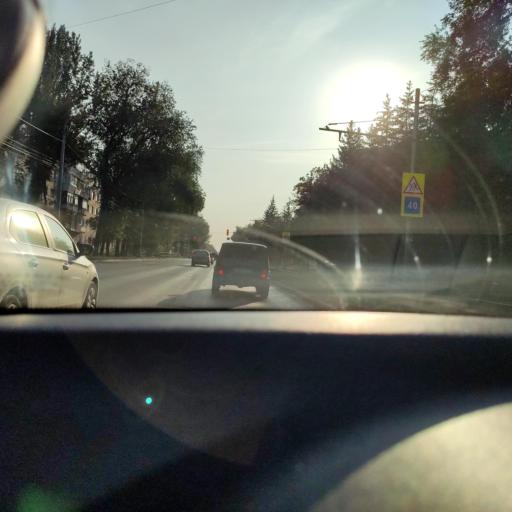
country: RU
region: Samara
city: Samara
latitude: 53.1997
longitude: 50.2251
